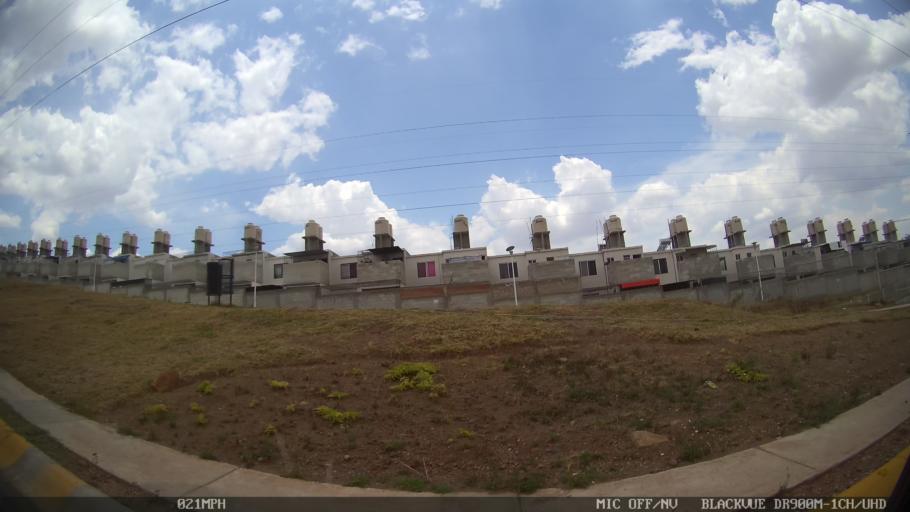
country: MX
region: Jalisco
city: Tonala
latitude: 20.6447
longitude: -103.2265
